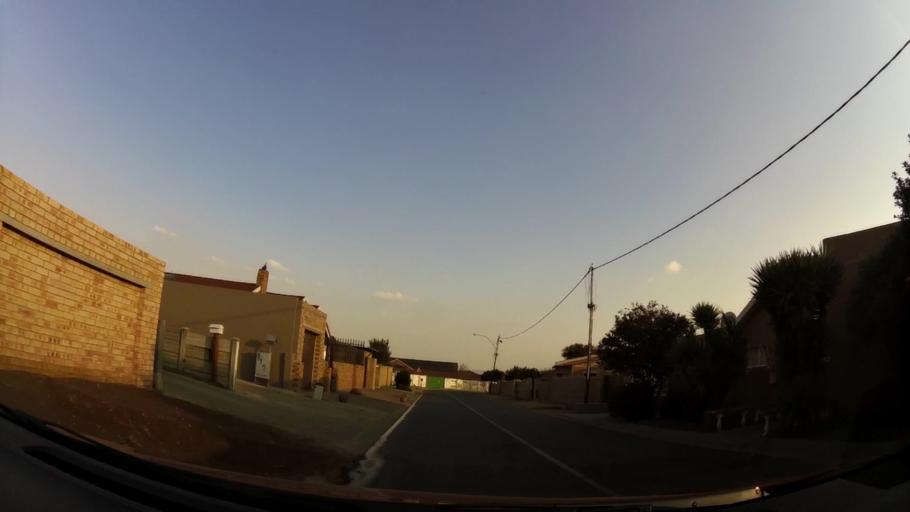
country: ZA
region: Gauteng
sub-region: City of Johannesburg Metropolitan Municipality
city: Soweto
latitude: -26.2822
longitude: 27.8978
